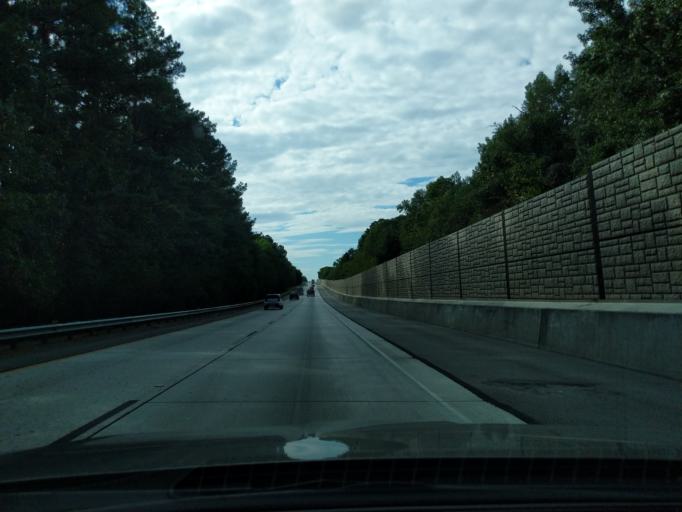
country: US
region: Georgia
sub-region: Columbia County
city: Grovetown
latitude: 33.4793
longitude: -82.1512
